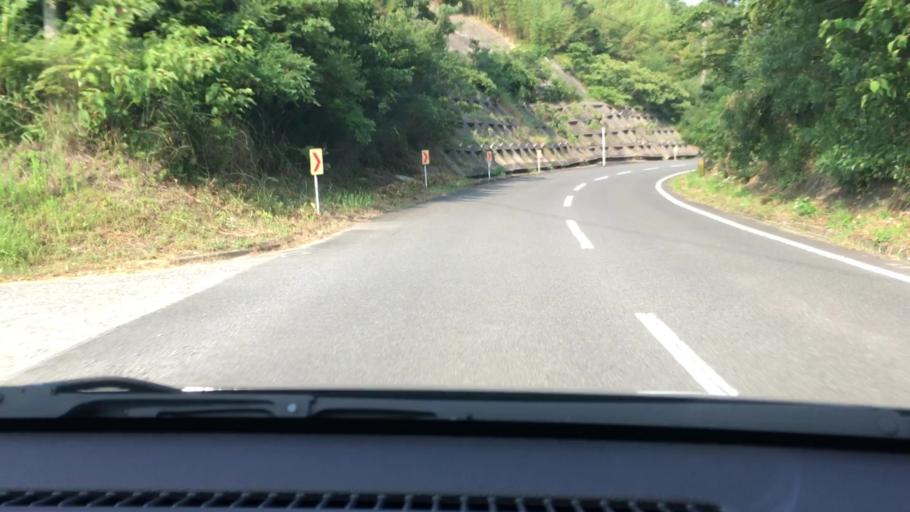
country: JP
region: Nagasaki
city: Sasebo
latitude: 32.9964
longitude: 129.7188
